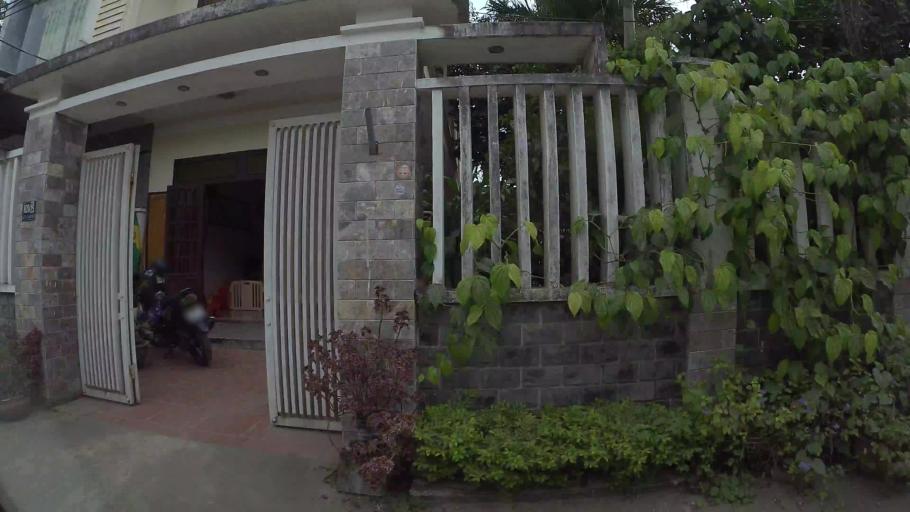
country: VN
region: Da Nang
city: Cam Le
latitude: 16.0336
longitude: 108.1791
